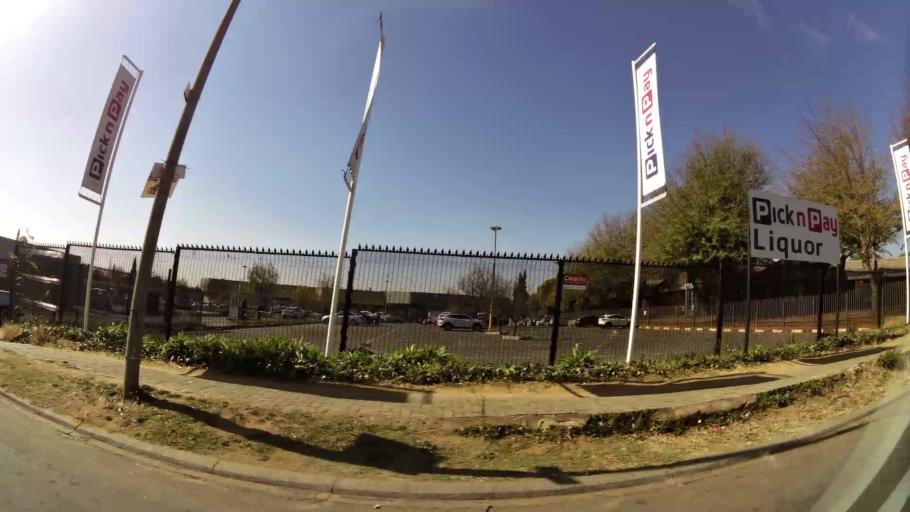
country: ZA
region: Gauteng
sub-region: Ekurhuleni Metropolitan Municipality
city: Tembisa
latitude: -26.0520
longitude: 28.2296
